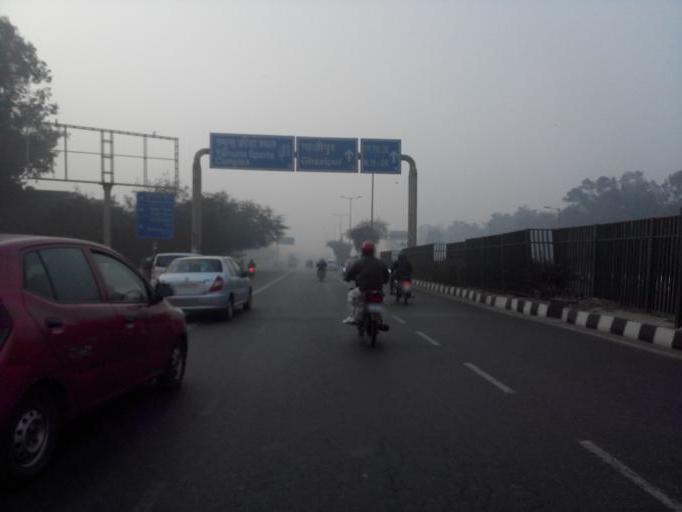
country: IN
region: Uttar Pradesh
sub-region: Gautam Buddha Nagar
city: Noida
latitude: 28.6596
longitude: 77.3201
